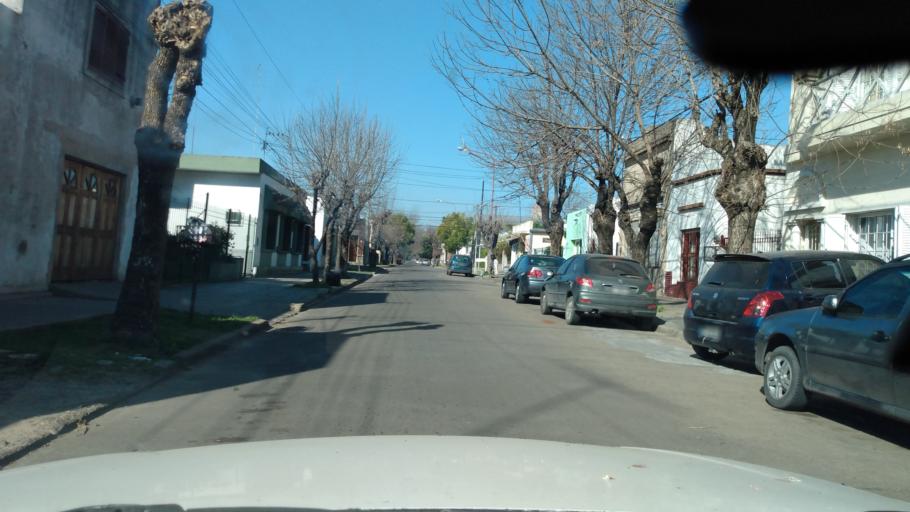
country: AR
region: Buenos Aires
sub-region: Partido de Lujan
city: Lujan
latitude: -34.5715
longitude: -59.1092
